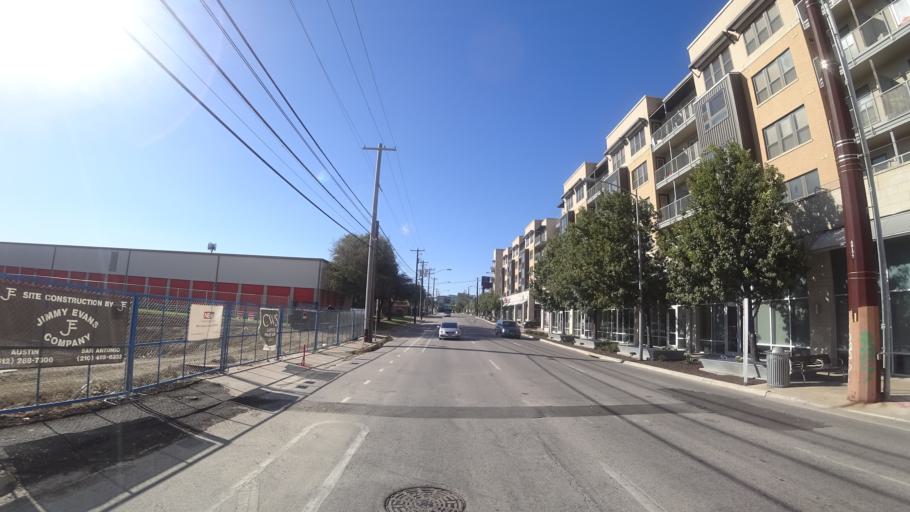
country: US
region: Texas
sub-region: Travis County
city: Austin
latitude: 30.2722
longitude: -97.7597
